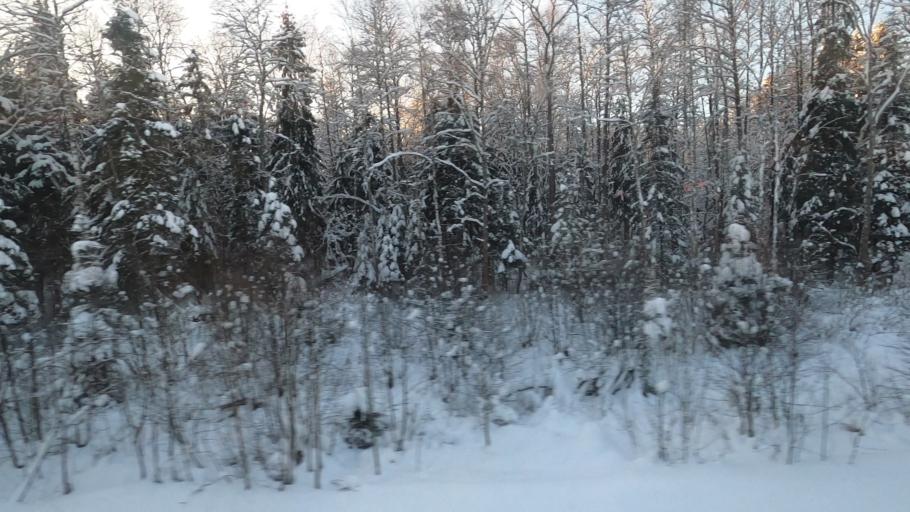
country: RU
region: Moskovskaya
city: Novo-Nikol'skoye
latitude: 56.5954
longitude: 37.5663
